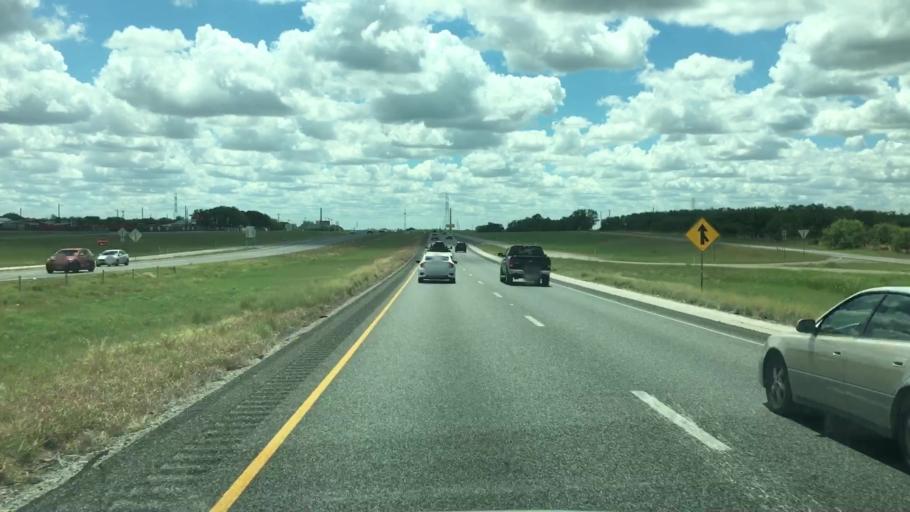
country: US
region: Texas
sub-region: Bexar County
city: Elmendorf
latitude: 29.2787
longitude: -98.3960
